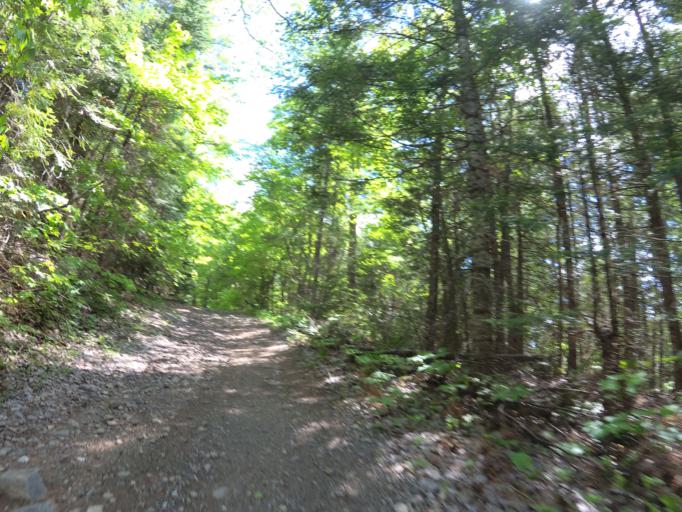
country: CA
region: Ontario
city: Renfrew
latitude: 45.0465
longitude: -76.8312
